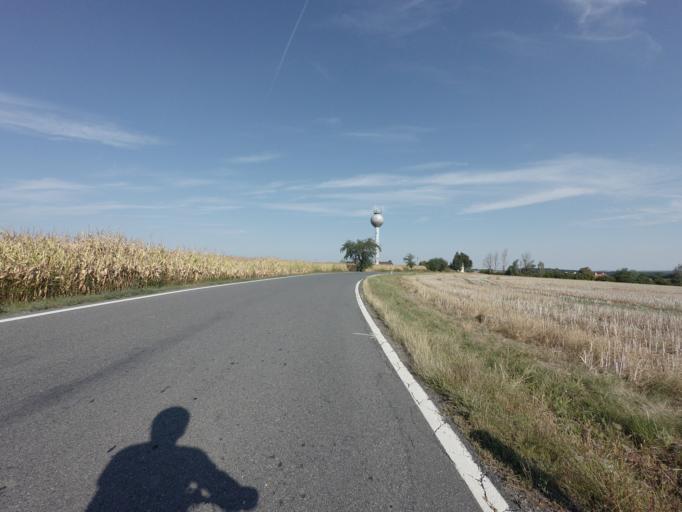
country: CZ
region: Jihocesky
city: Bernartice
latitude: 49.3017
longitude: 14.3824
